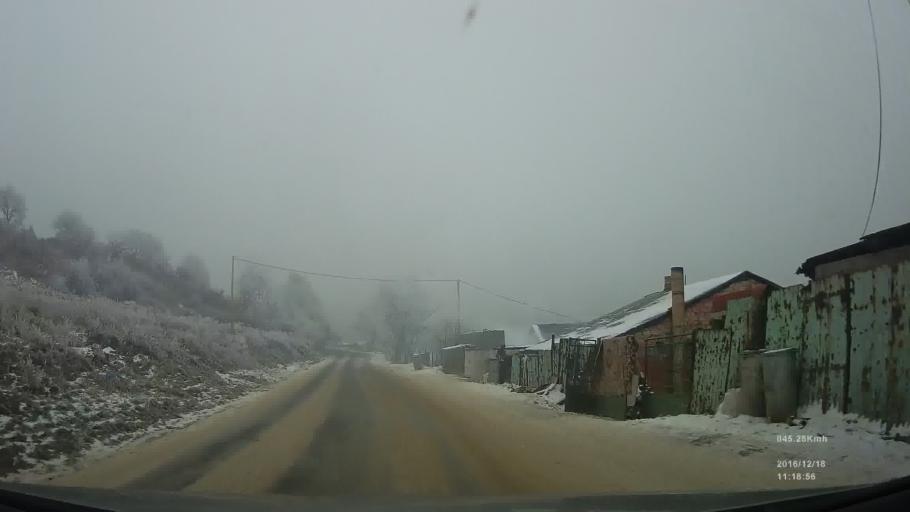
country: SK
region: Presovsky
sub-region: Okres Presov
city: Presov
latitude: 48.9141
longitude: 21.3472
